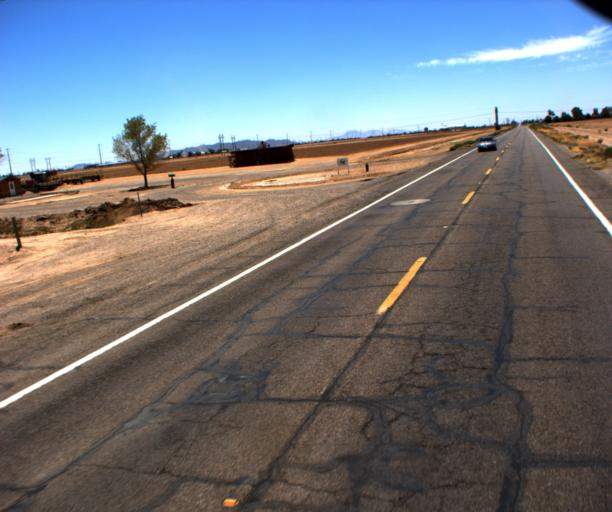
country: US
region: Arizona
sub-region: Pinal County
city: Coolidge
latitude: 32.8795
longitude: -111.5580
